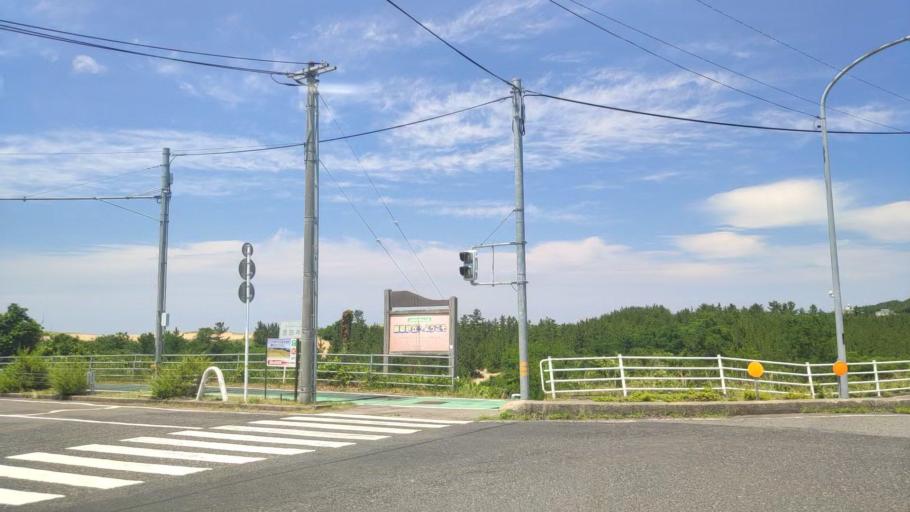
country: JP
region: Tottori
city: Tottori
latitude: 35.5337
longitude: 134.2305
